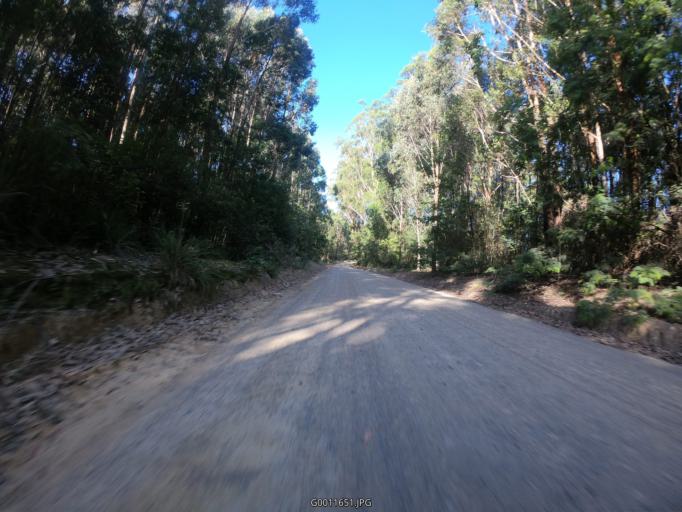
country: AU
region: New South Wales
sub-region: Lake Macquarie Shire
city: Cooranbong
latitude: -33.0484
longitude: 151.3131
